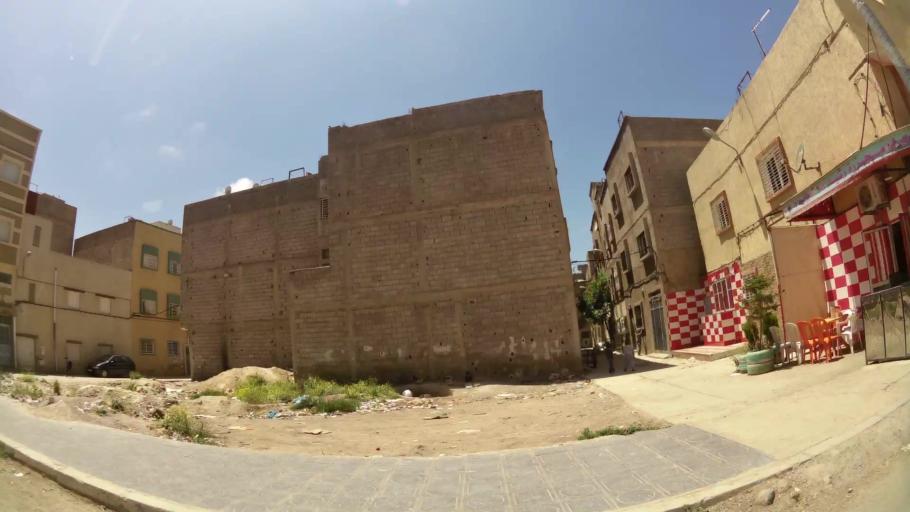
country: MA
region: Fes-Boulemane
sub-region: Fes
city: Fes
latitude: 34.0381
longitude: -5.0505
